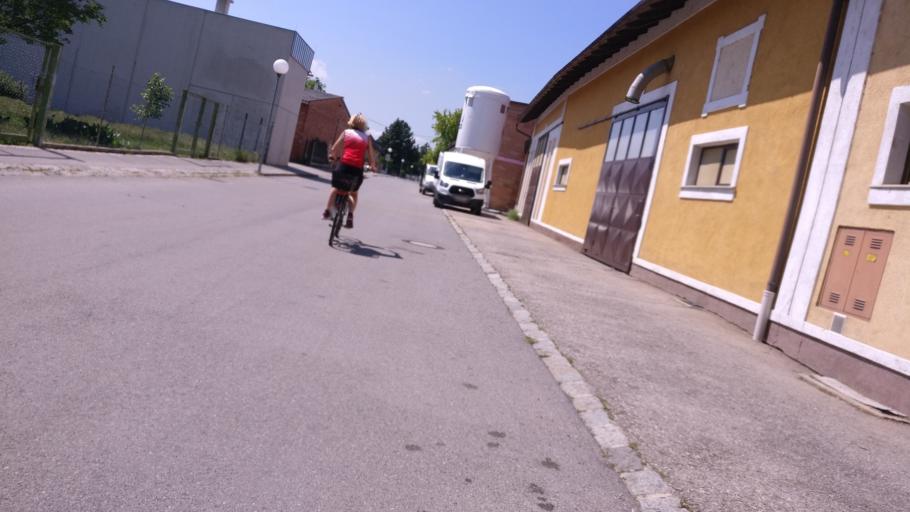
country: AT
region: Lower Austria
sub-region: Politischer Bezirk Baden
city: Oberwaltersdorf
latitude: 47.9791
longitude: 16.3259
